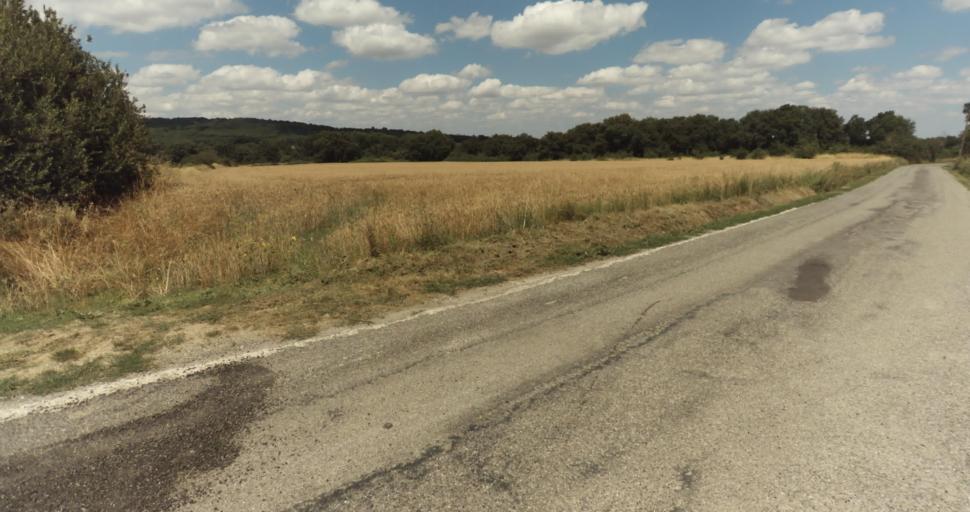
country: FR
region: Midi-Pyrenees
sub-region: Departement du Gers
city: Pujaudran
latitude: 43.5612
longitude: 1.1590
